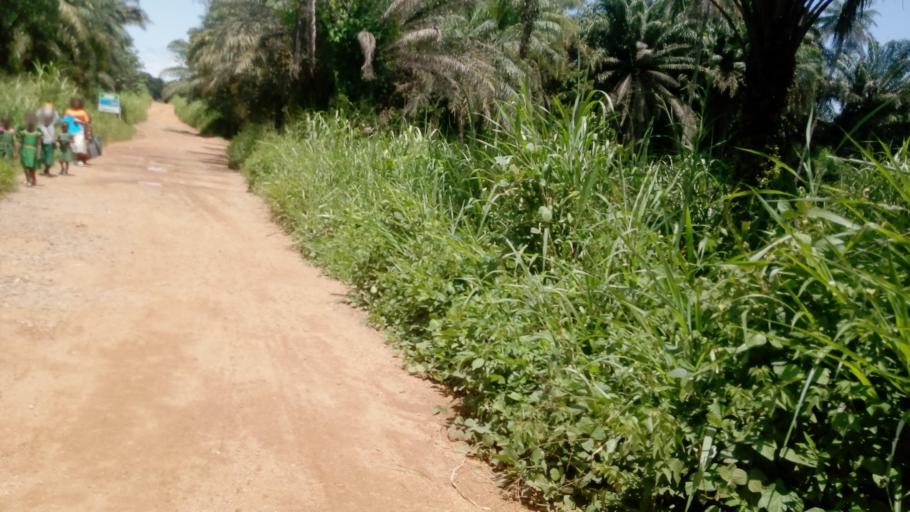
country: SL
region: Northern Province
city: Binkolo
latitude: 8.9572
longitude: -11.9637
